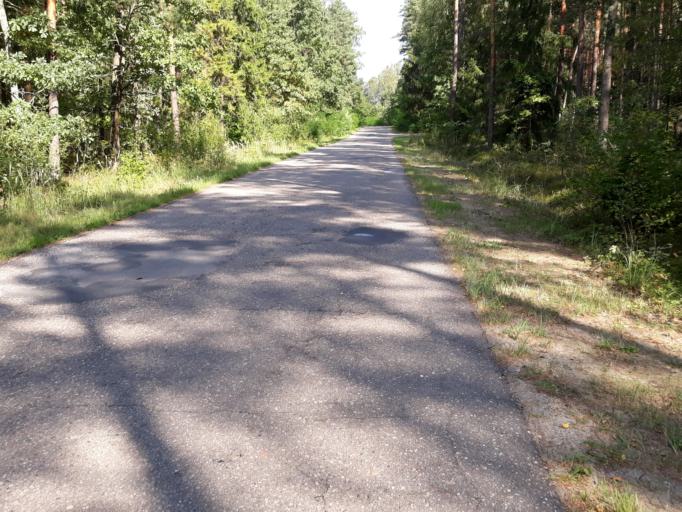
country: PL
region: Lublin Voivodeship
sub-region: Powiat janowski
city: Dzwola
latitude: 50.6479
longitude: 22.5978
